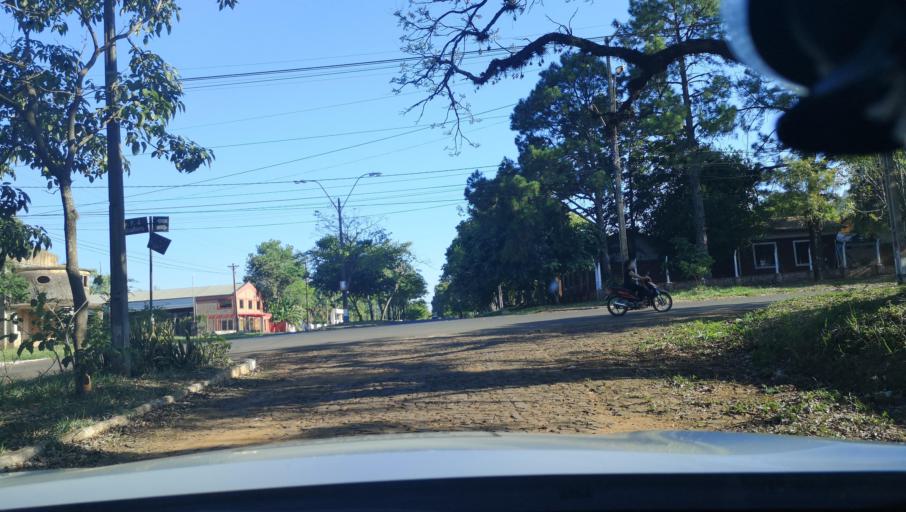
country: PY
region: Itapua
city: Carmen del Parana
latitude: -27.1640
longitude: -56.2419
